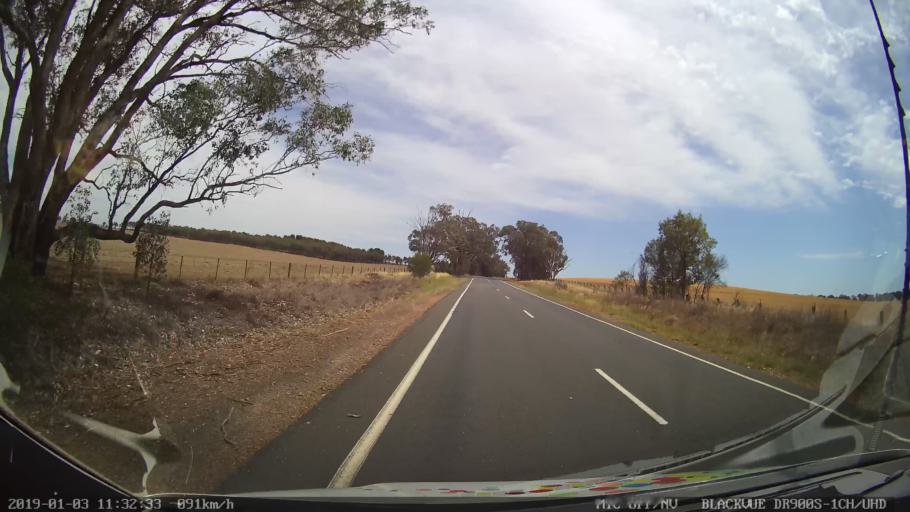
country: AU
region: New South Wales
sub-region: Weddin
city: Grenfell
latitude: -33.9568
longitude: 148.1778
